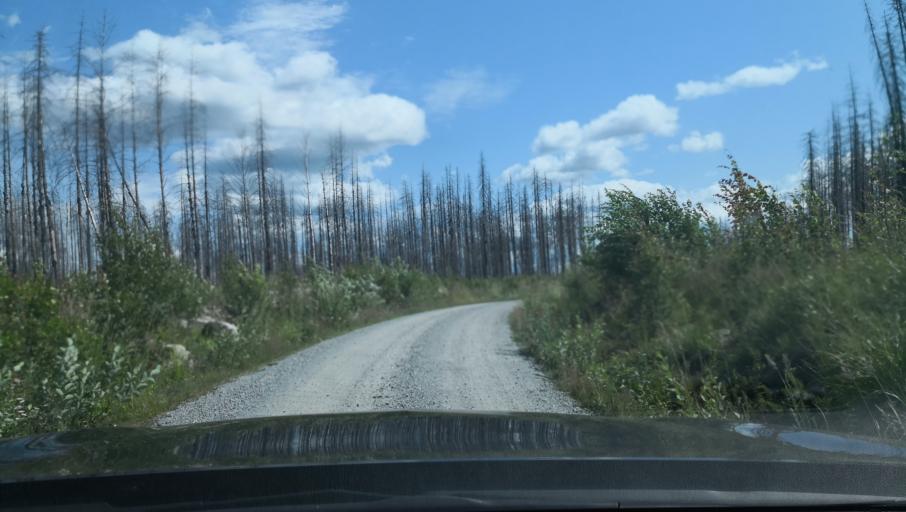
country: SE
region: Vaestmanland
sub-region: Surahammars Kommun
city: Ramnas
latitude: 59.8978
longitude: 16.1372
